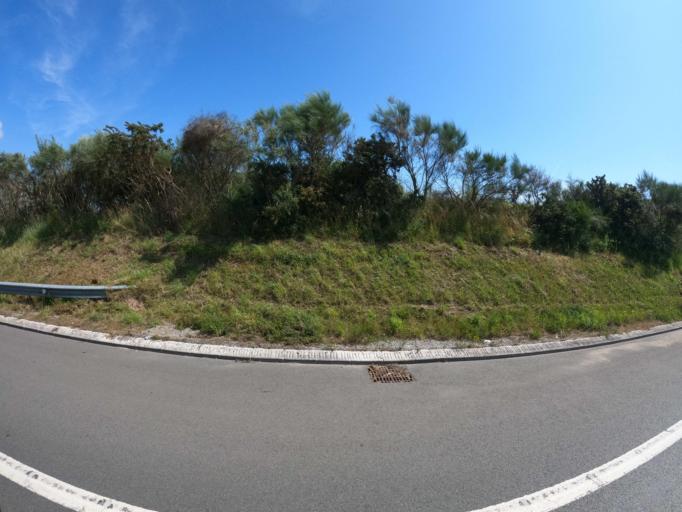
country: FR
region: Pays de la Loire
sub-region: Departement de la Loire-Atlantique
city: Saint-Nazaire
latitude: 47.2861
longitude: -2.2493
